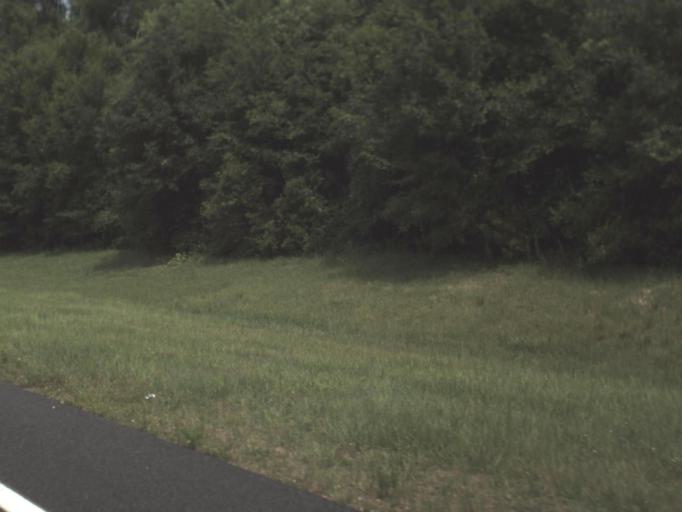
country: US
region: Florida
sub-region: Alachua County
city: Gainesville
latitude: 29.6068
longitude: -82.2255
